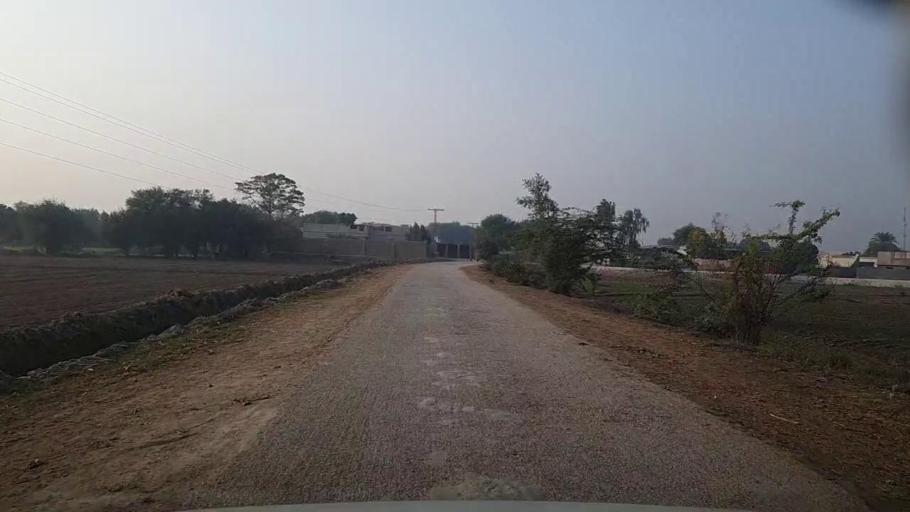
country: PK
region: Sindh
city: Kandiari
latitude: 27.0045
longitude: 68.4643
